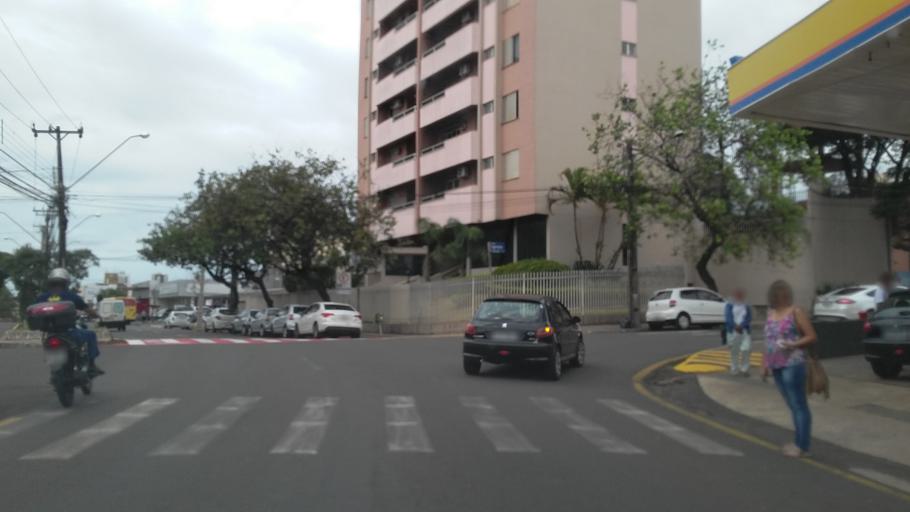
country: BR
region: Parana
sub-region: Londrina
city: Londrina
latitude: -23.3228
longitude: -51.1676
